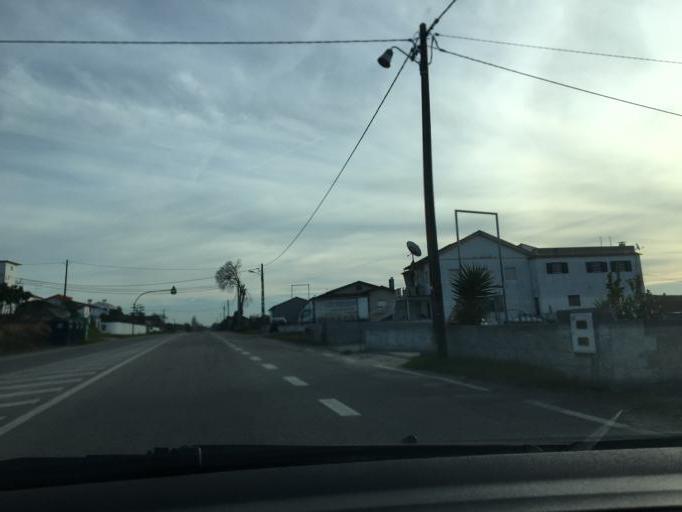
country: PT
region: Coimbra
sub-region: Soure
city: Alfarelos
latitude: 40.2086
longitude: -8.6239
